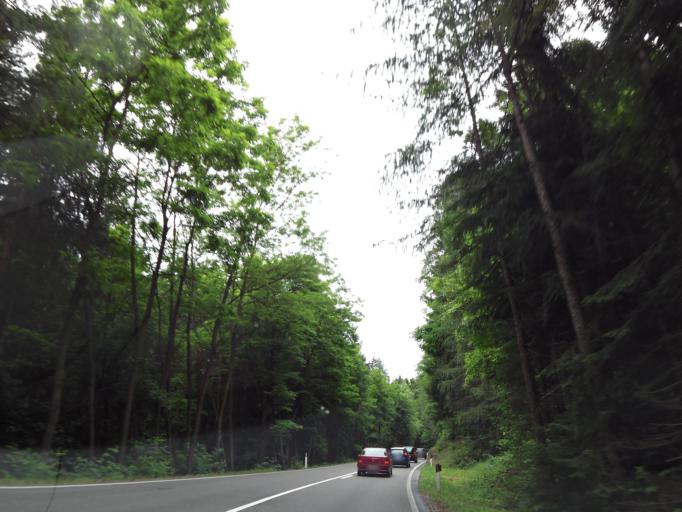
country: IT
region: Trentino-Alto Adige
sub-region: Bolzano
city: Fie Allo Sciliar
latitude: 46.5330
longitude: 11.5155
